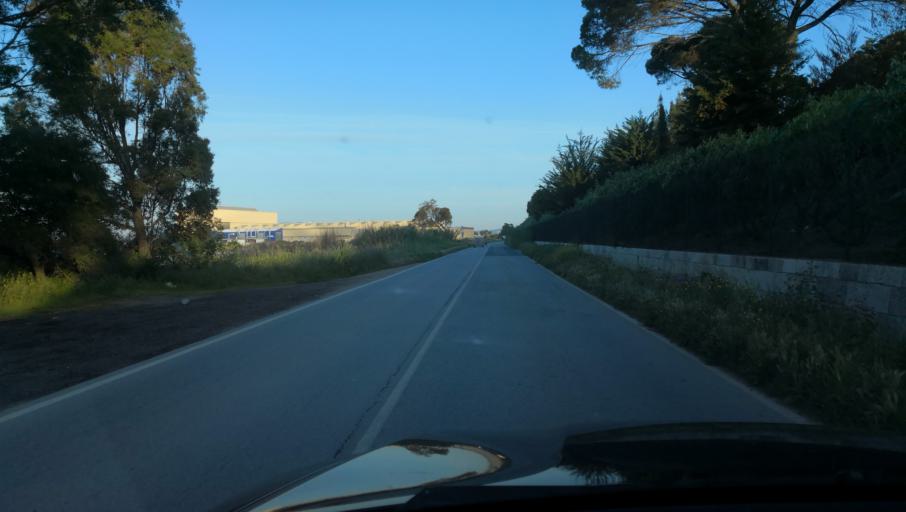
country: PT
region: Setubal
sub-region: Setubal
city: Setubal
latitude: 38.4892
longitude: -8.8120
